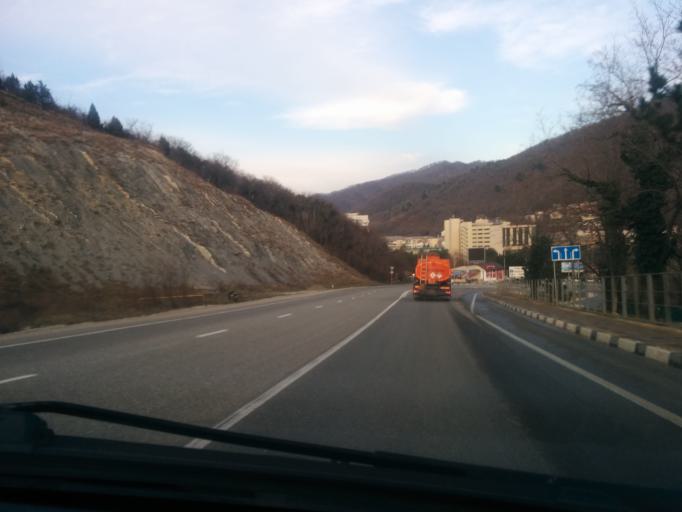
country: RU
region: Krasnodarskiy
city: Nebug
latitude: 44.1656
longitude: 38.9962
